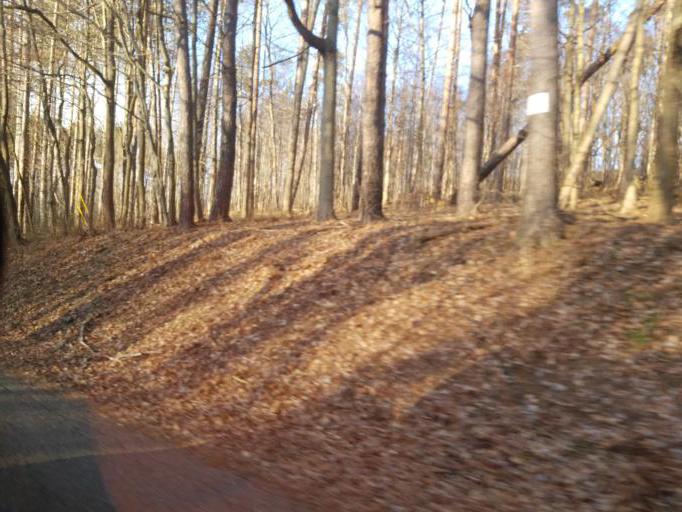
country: US
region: Ohio
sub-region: Sandusky County
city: Bellville
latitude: 40.5893
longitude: -82.3870
